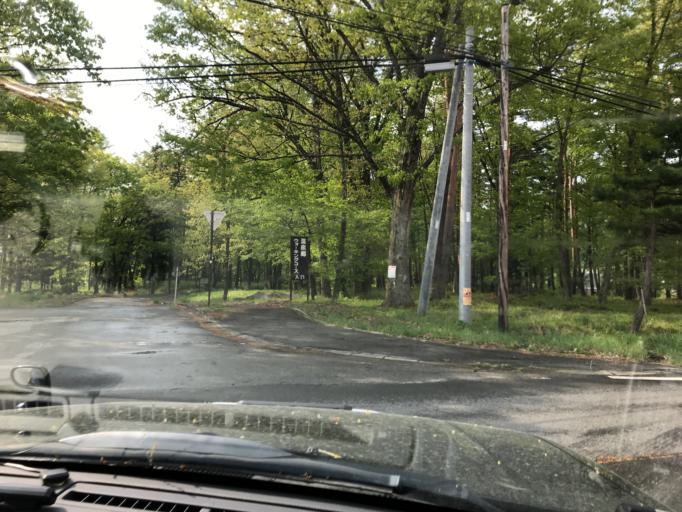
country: JP
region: Nagano
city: Omachi
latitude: 36.5266
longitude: 137.8118
